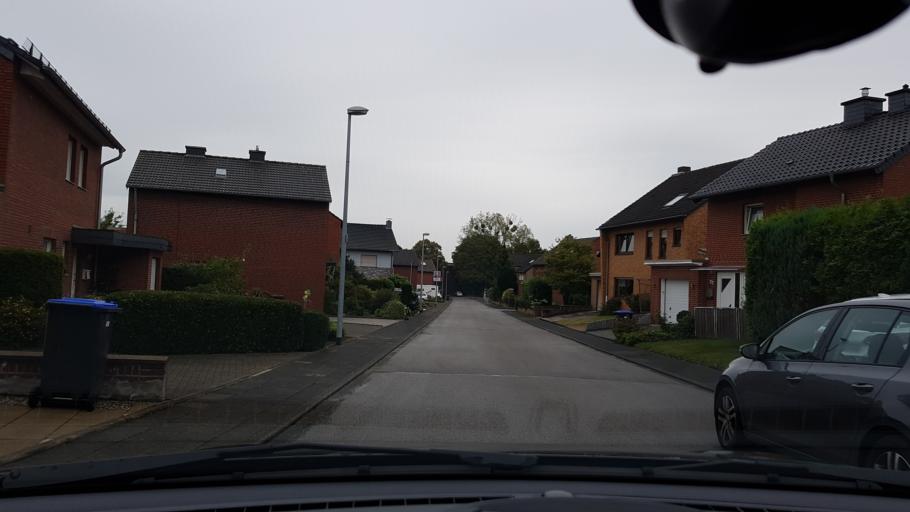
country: DE
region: North Rhine-Westphalia
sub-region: Regierungsbezirk Koln
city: Bedburg
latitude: 51.0022
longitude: 6.5546
